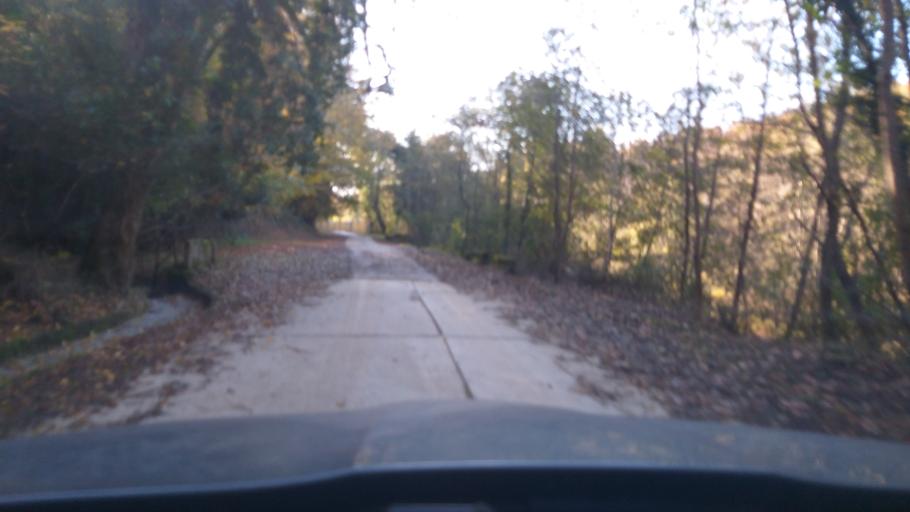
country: GE
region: Abkhazia
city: Bich'vinta
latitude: 43.1623
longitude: 40.4626
